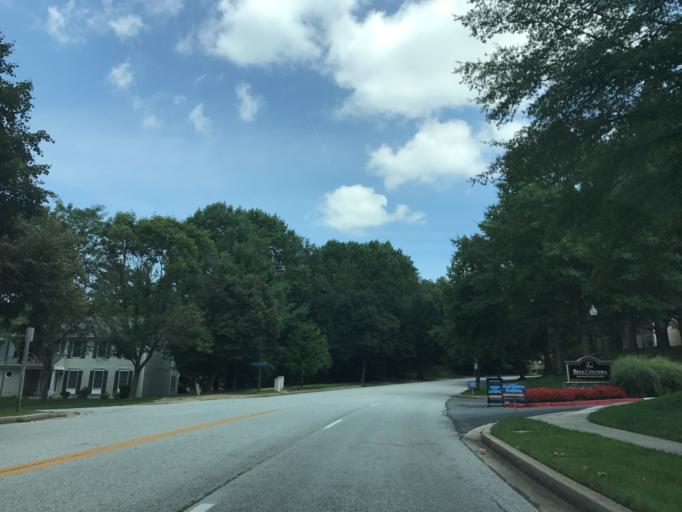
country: US
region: Maryland
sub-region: Howard County
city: Riverside
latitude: 39.2121
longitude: -76.9012
